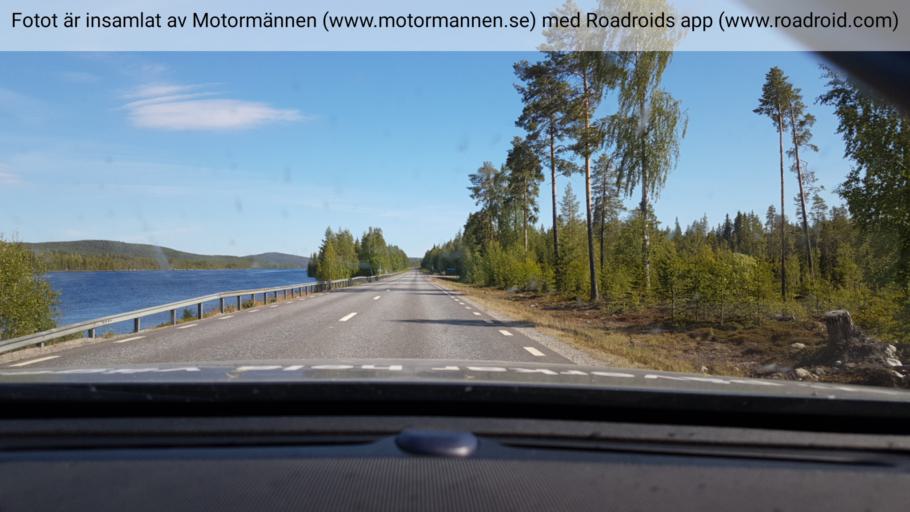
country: SE
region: Vaesterbotten
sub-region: Lycksele Kommun
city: Soderfors
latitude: 64.7489
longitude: 18.1869
